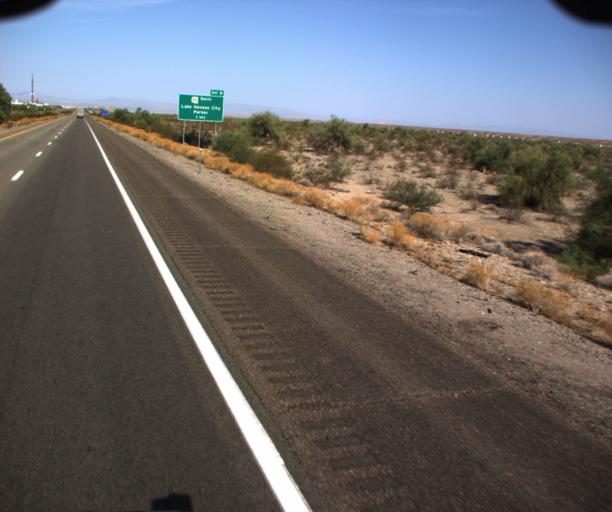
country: US
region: Arizona
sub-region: Mohave County
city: Desert Hills
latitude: 34.7304
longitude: -114.2954
